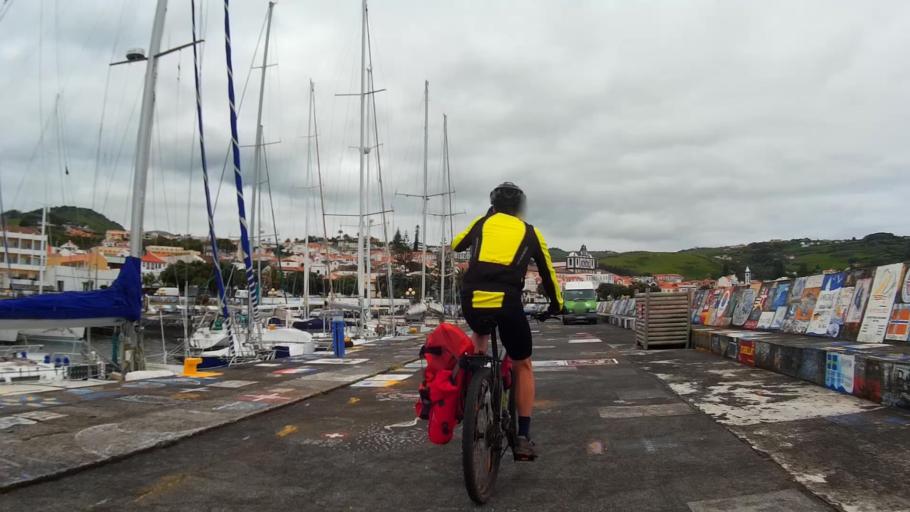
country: PT
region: Azores
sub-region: Horta
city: Horta
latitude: 38.5337
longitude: -28.6250
